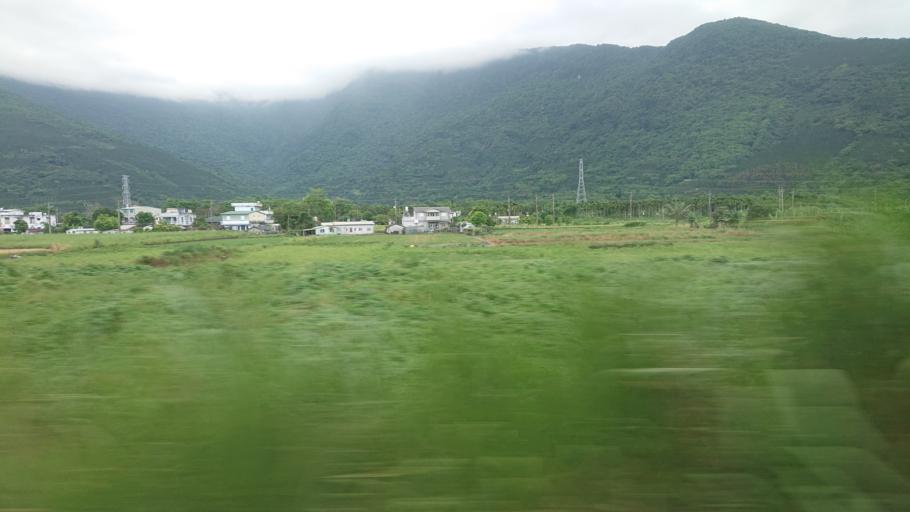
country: TW
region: Taiwan
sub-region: Hualien
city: Hualian
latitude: 23.7511
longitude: 121.4494
